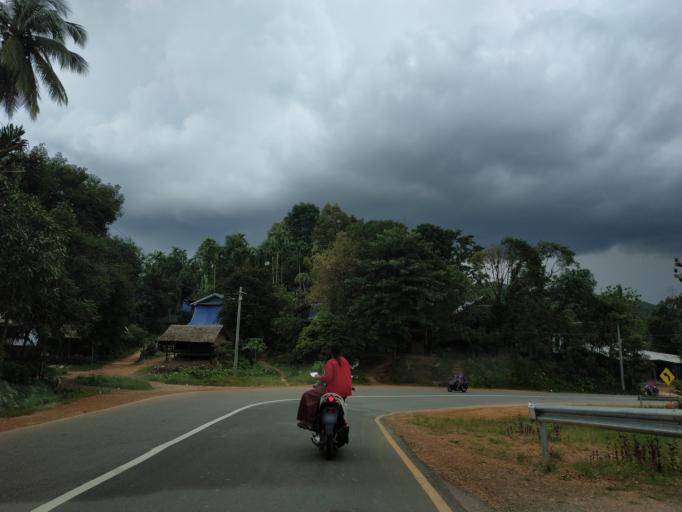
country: MM
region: Tanintharyi
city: Dawei
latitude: 13.9566
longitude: 98.2427
